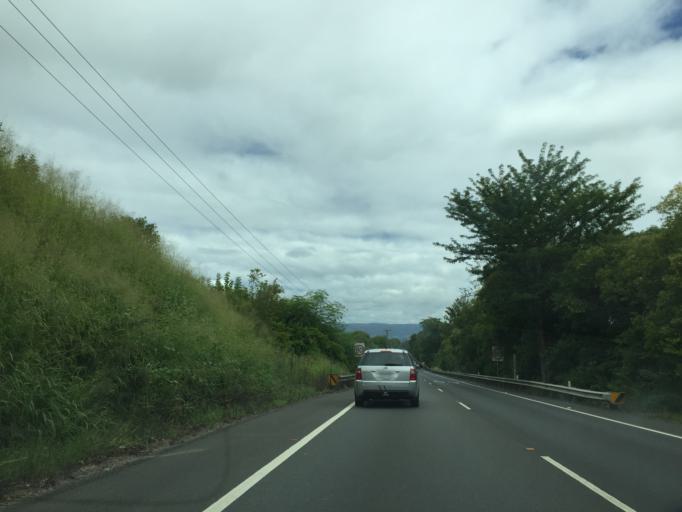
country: AU
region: New South Wales
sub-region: Hawkesbury
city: Richmond
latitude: -33.5946
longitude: 150.7421
